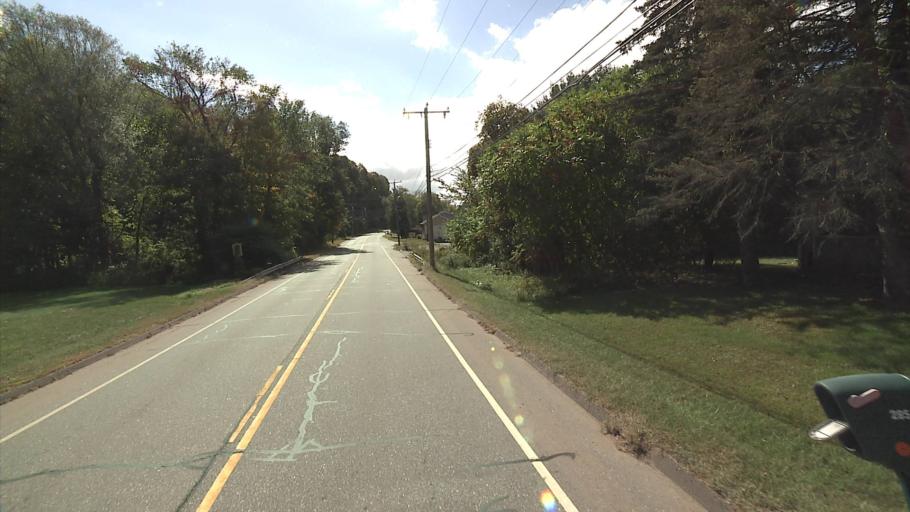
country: US
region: Connecticut
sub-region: Middlesex County
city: Durham
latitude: 41.5216
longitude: -72.7288
